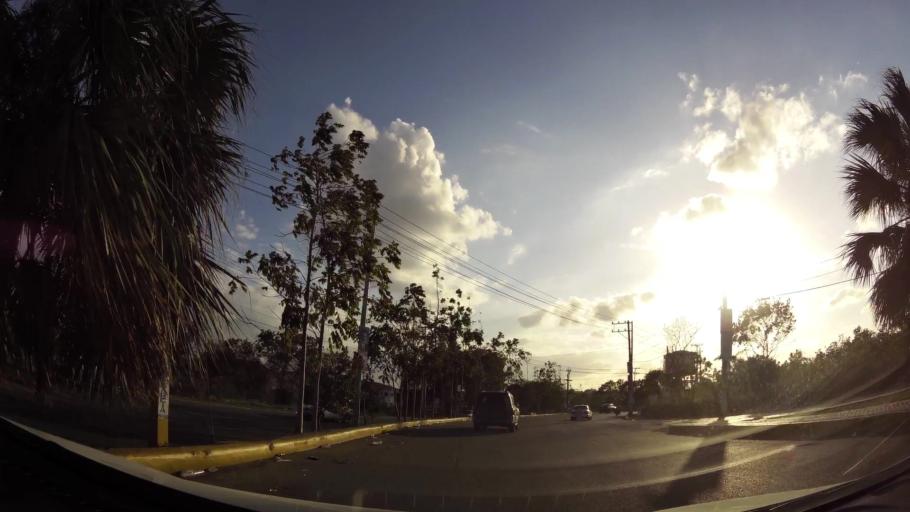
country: DO
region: Nacional
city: La Agustina
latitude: 18.5470
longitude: -69.9212
